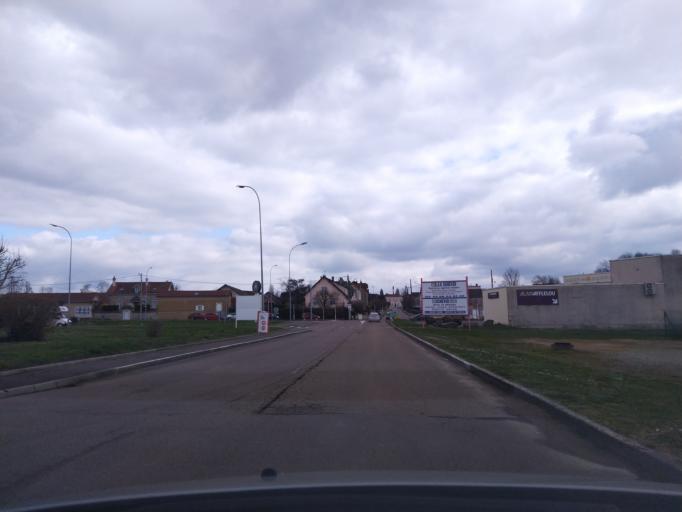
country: FR
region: Bourgogne
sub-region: Departement de l'Yonne
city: Avallon
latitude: 47.4968
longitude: 3.9069
